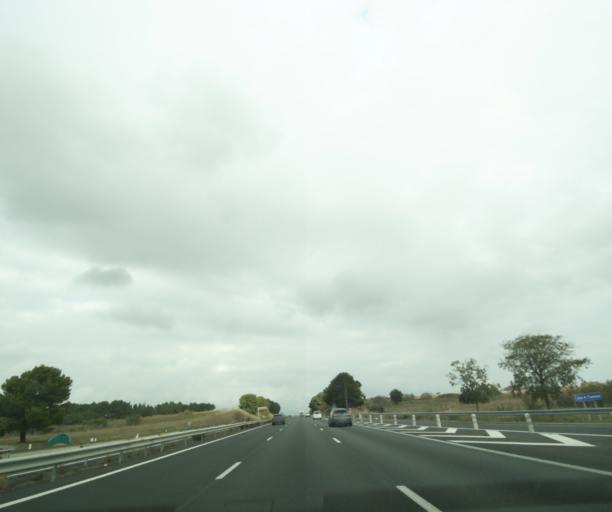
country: FR
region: Languedoc-Roussillon
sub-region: Departement de l'Herault
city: Florensac
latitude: 43.3973
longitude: 3.4704
